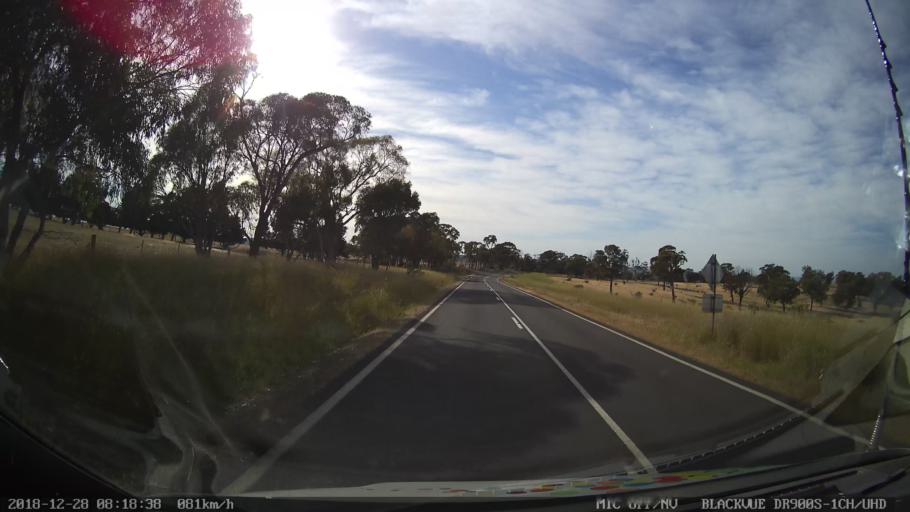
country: AU
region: New South Wales
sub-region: Blayney
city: Blayney
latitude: -33.8495
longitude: 149.3489
